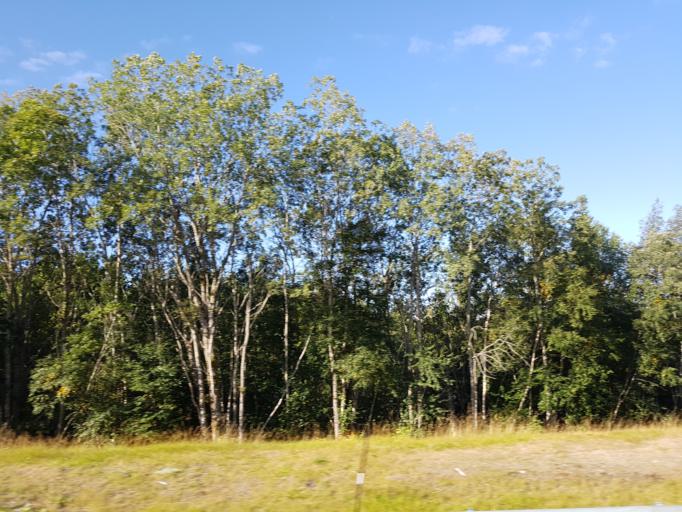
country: NO
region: Sor-Trondelag
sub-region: Trondheim
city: Trondheim
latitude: 63.6420
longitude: 10.2696
